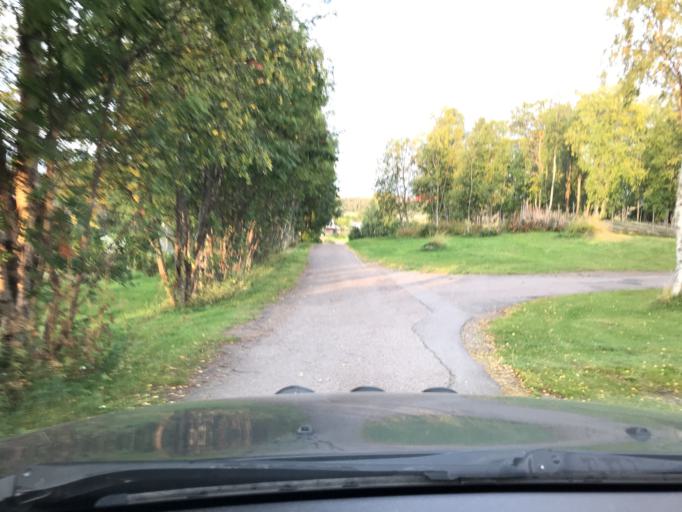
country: SE
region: Norrbotten
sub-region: Gallivare Kommun
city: Malmberget
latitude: 67.6481
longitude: 21.0545
